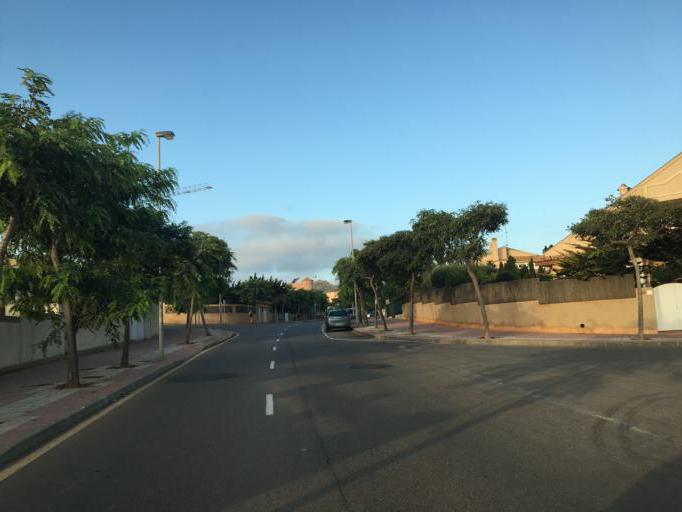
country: ES
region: Murcia
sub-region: Murcia
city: La Manga del Mar Menor
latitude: 37.6260
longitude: -0.7066
